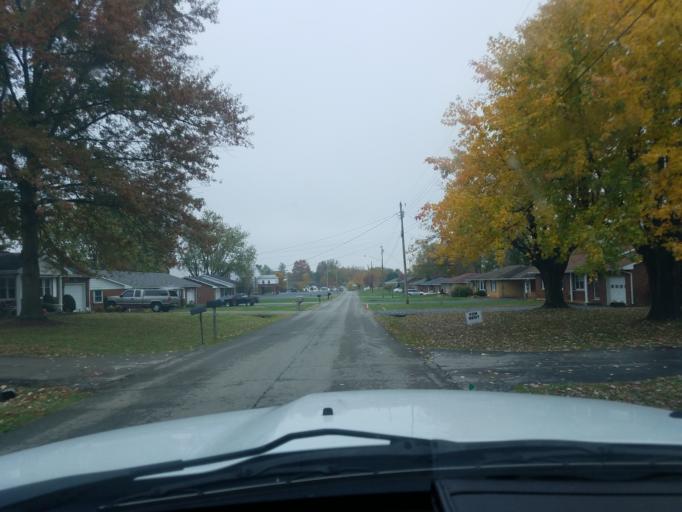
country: US
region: Kentucky
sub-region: Taylor County
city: Campbellsville
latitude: 37.3543
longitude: -85.3377
